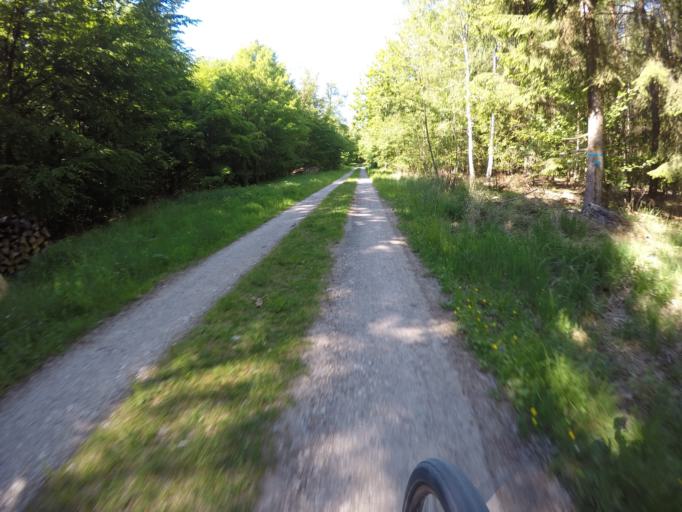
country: DE
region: Baden-Wuerttemberg
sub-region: Regierungsbezirk Stuttgart
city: Sindelfingen
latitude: 48.7417
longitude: 9.0433
